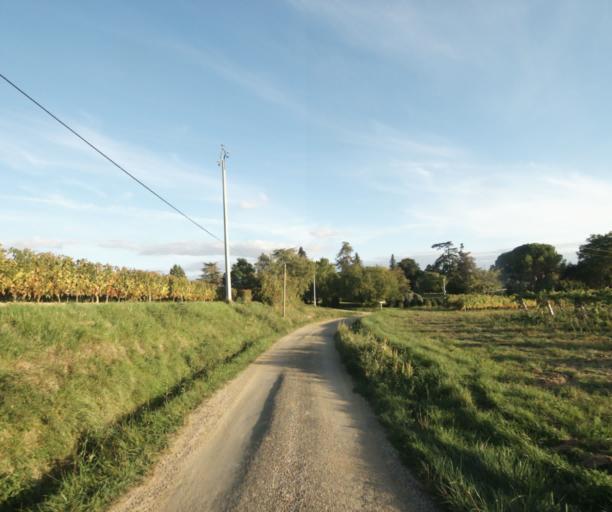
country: FR
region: Midi-Pyrenees
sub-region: Departement du Gers
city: Gondrin
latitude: 43.8642
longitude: 0.2949
